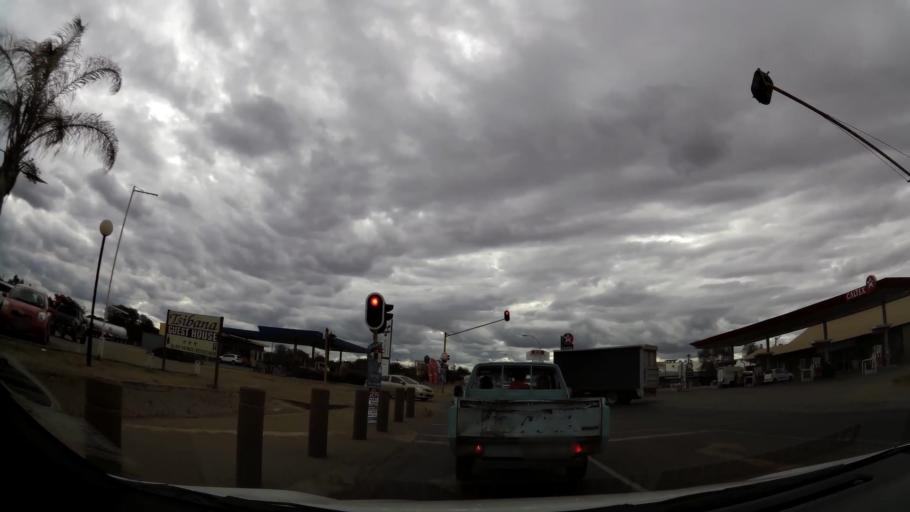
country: ZA
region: Limpopo
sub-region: Waterberg District Municipality
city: Modimolle
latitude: -24.7110
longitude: 28.4157
